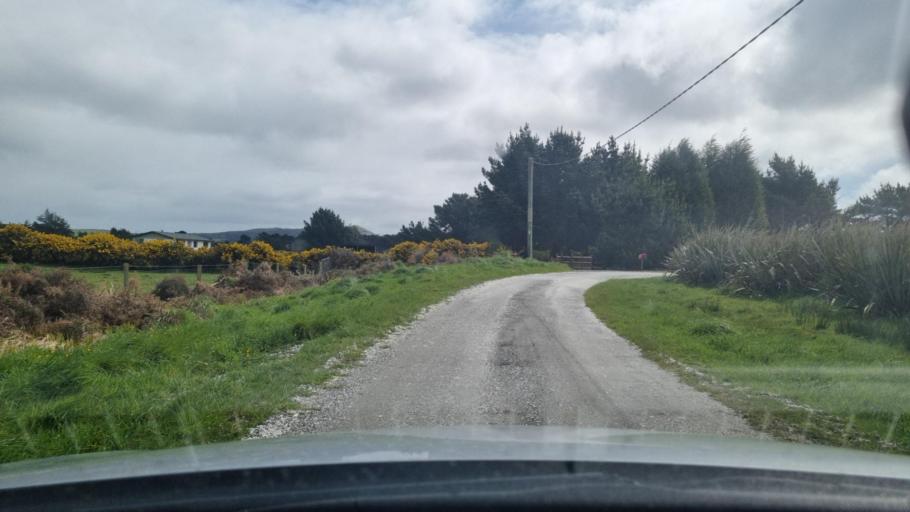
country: NZ
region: Southland
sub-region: Invercargill City
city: Bluff
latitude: -46.5389
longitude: 168.2998
